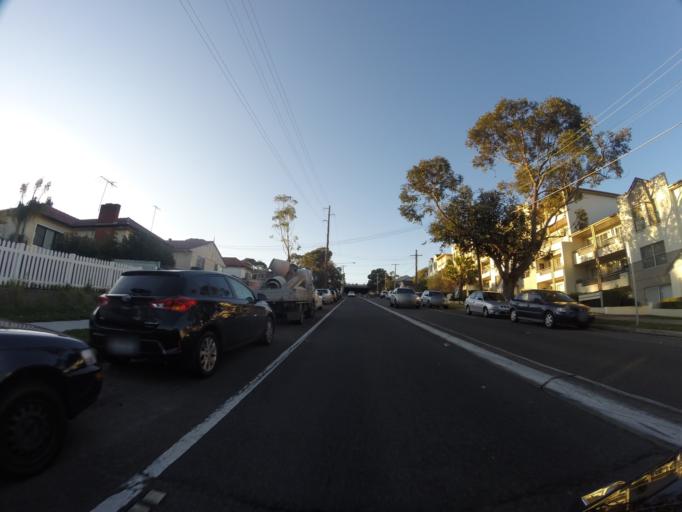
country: AU
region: New South Wales
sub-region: Sutherland Shire
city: Miranda
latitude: -34.0373
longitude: 151.0979
